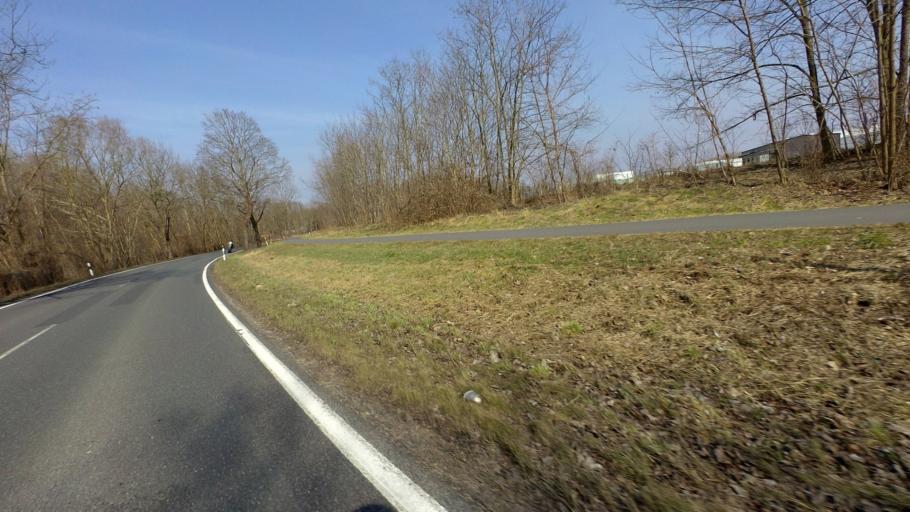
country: DE
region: Brandenburg
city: Werder
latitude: 52.4004
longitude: 12.9068
